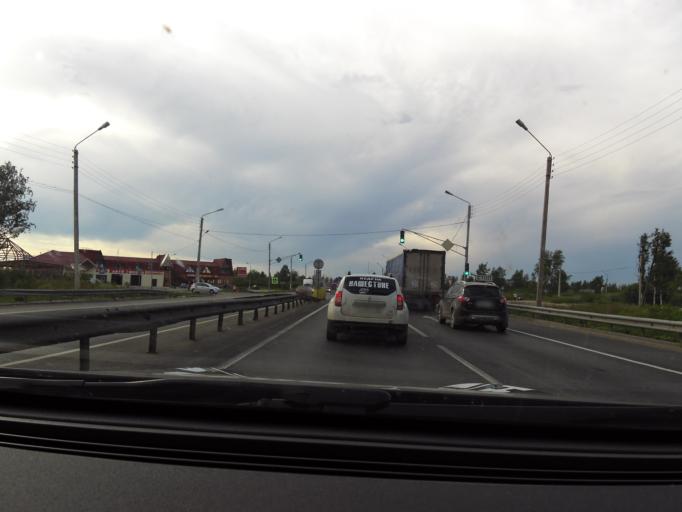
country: RU
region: Vladimir
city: Vyazniki
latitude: 56.2349
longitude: 42.1121
